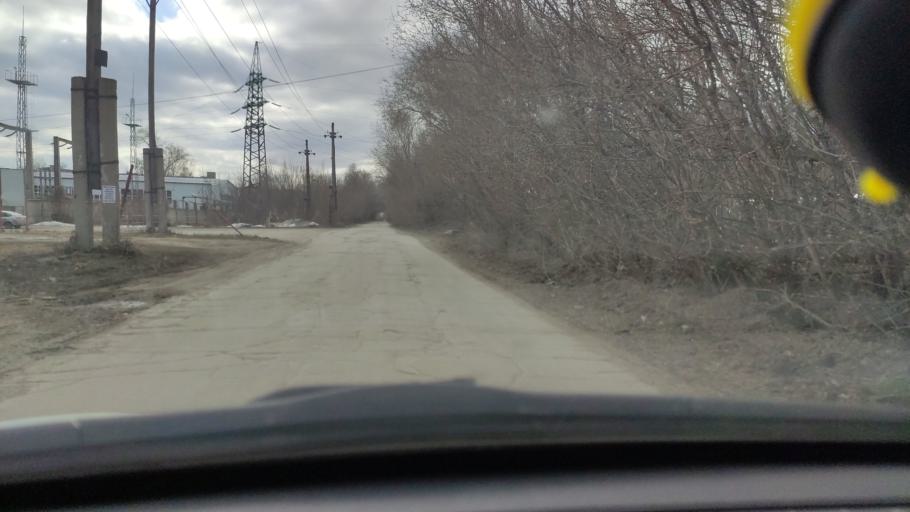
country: RU
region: Samara
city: Tol'yatti
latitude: 53.5222
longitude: 49.4551
